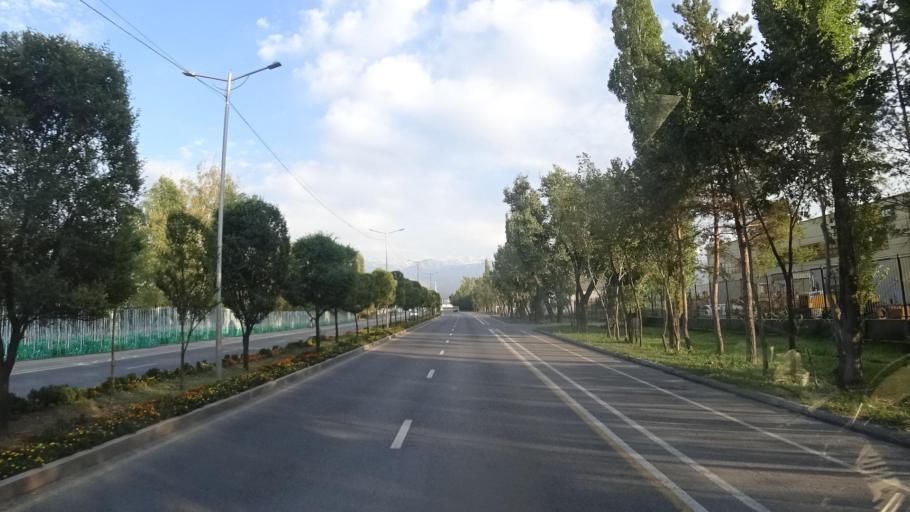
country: KZ
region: Almaty Oblysy
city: Pervomayskiy
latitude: 43.3341
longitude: 77.0042
